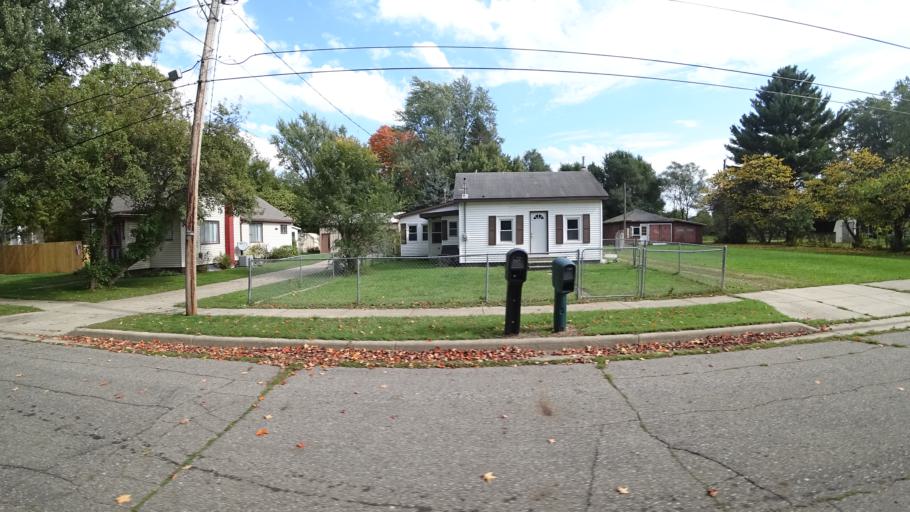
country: US
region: Michigan
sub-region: Saint Joseph County
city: Three Rivers
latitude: 41.9373
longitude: -85.6212
